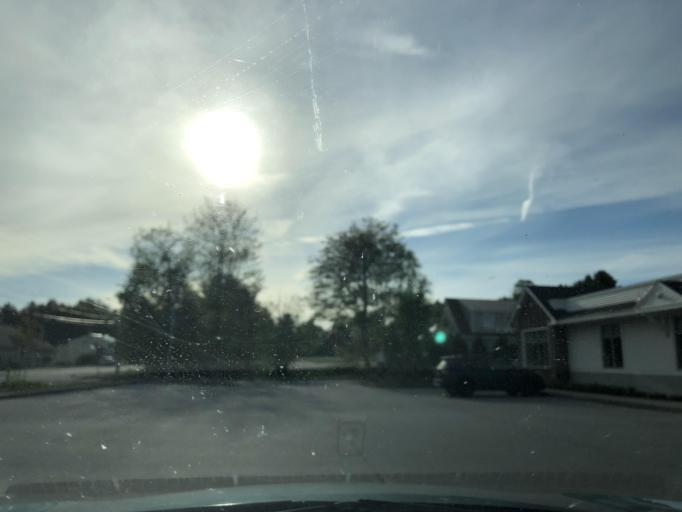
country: US
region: New Hampshire
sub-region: Merrimack County
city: New London
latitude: 43.4219
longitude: -71.9954
